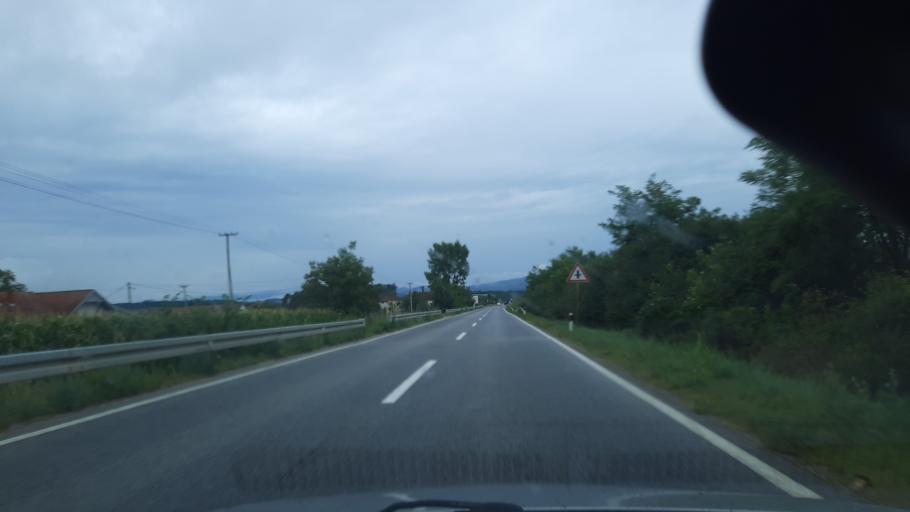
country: RS
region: Central Serbia
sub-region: Sumadijski Okrug
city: Knic
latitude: 43.9250
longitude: 20.7740
